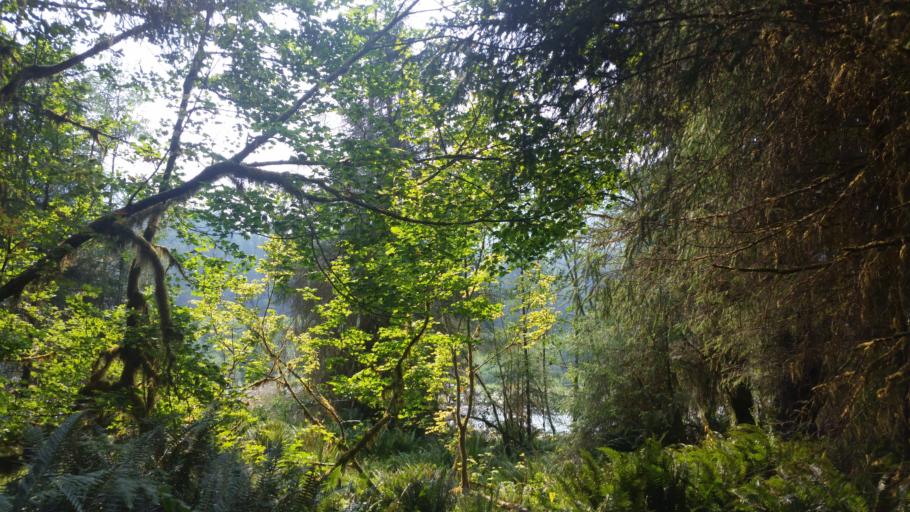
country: US
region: Washington
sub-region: Clallam County
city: Forks
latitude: 47.8591
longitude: -123.9271
